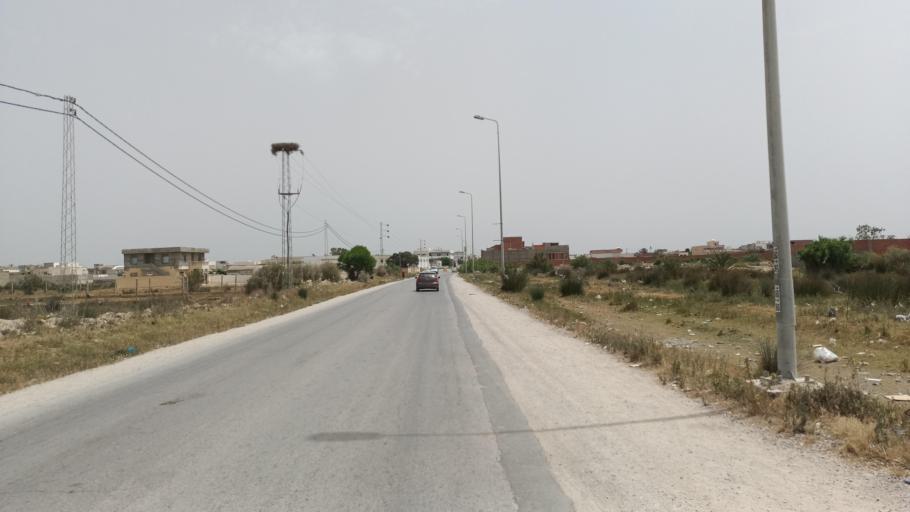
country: TN
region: Nabul
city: Manzil Bu Zalafah
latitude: 36.7099
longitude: 10.4830
